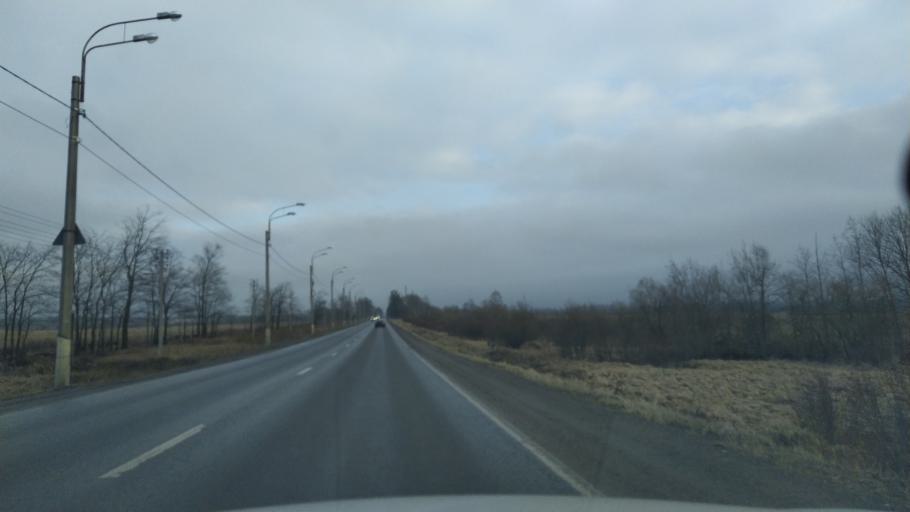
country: RU
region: St.-Petersburg
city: Aleksandrovskaya
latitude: 59.7114
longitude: 30.3139
